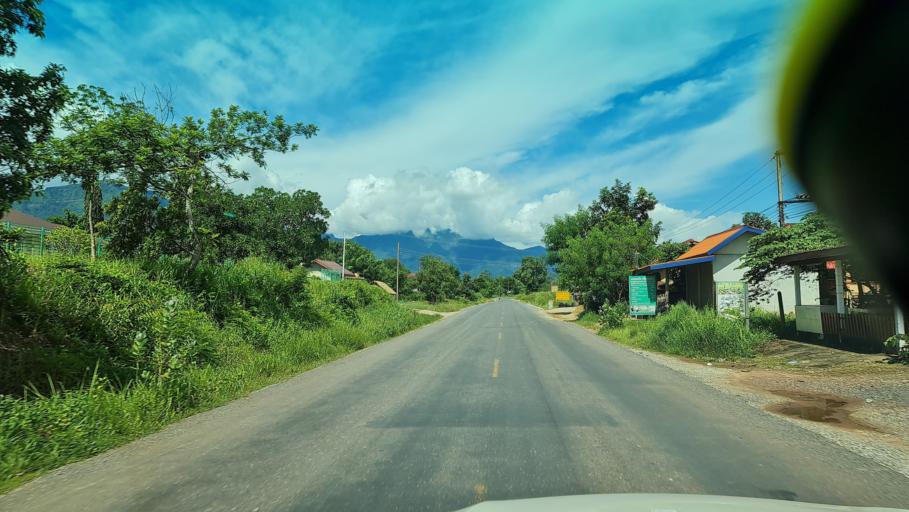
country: LA
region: Bolikhamxai
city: Ban Nahin
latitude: 18.3003
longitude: 104.1235
